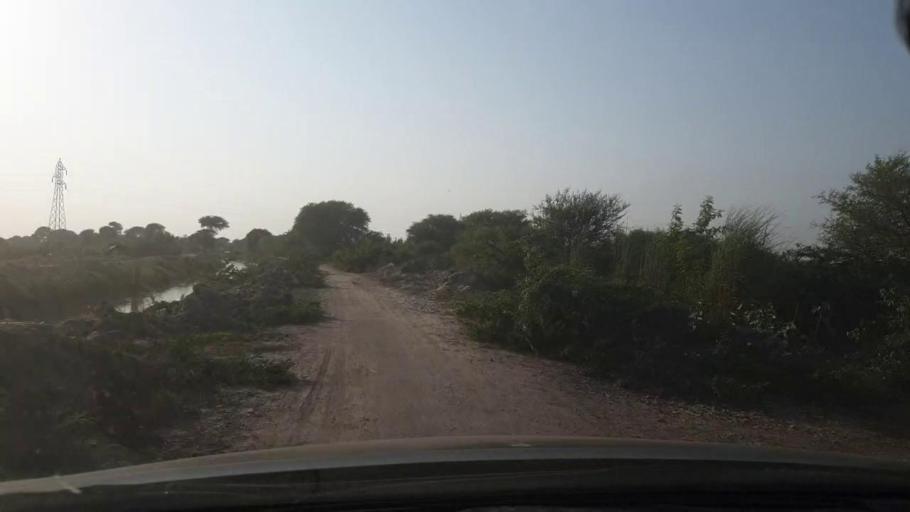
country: PK
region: Sindh
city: Naukot
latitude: 24.7663
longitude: 69.2249
